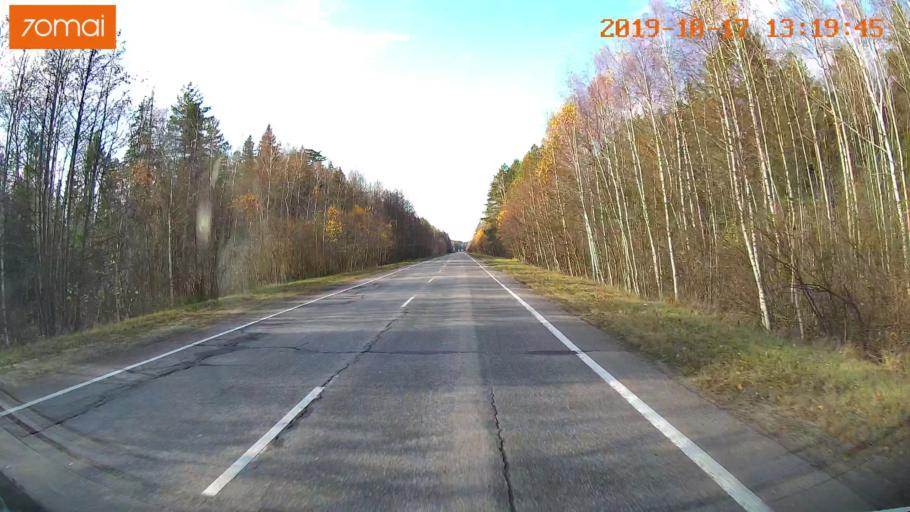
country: RU
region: Rjazan
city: Gus'-Zheleznyy
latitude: 55.0714
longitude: 41.0665
